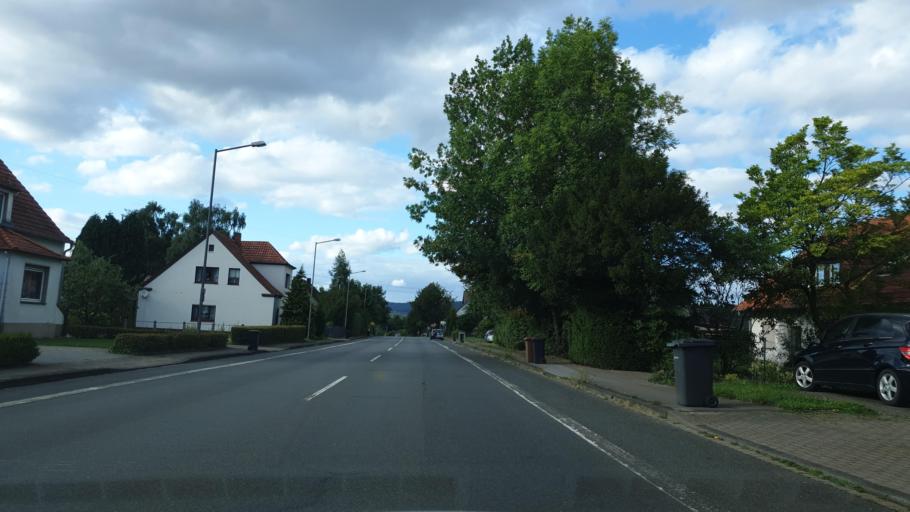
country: DE
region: North Rhine-Westphalia
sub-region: Regierungsbezirk Detmold
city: Huellhorst
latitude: 52.2429
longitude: 8.7039
